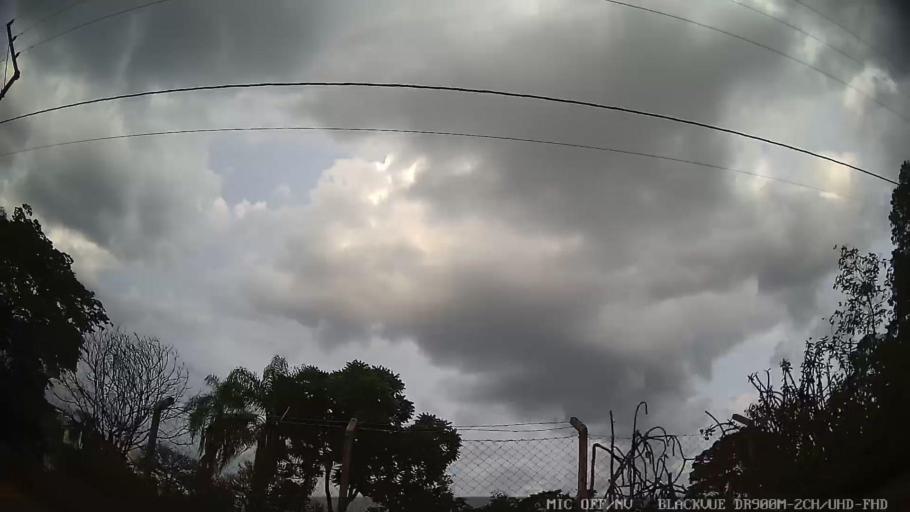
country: BR
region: Sao Paulo
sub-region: Braganca Paulista
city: Braganca Paulista
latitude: -22.9193
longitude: -46.5371
